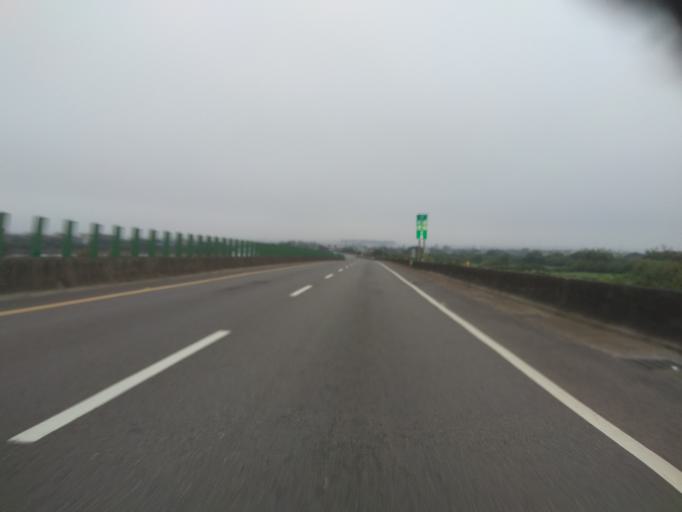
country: TW
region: Taiwan
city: Taoyuan City
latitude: 24.9686
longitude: 121.1340
